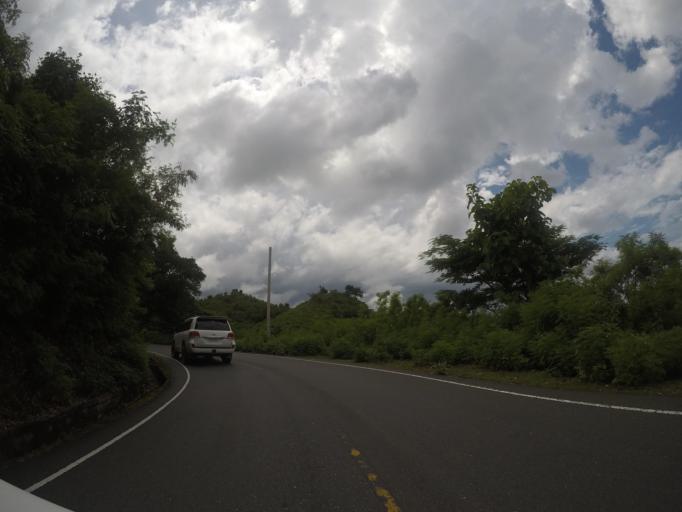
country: TL
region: Bobonaro
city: Maliana
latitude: -8.9577
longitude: 125.0606
